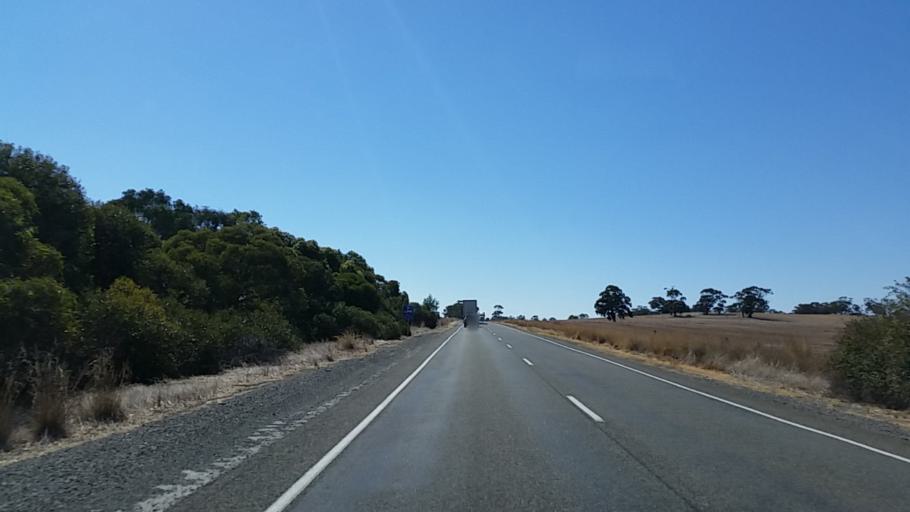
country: AU
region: South Australia
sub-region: Clare and Gilbert Valleys
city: Clare
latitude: -34.0539
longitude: 138.7961
